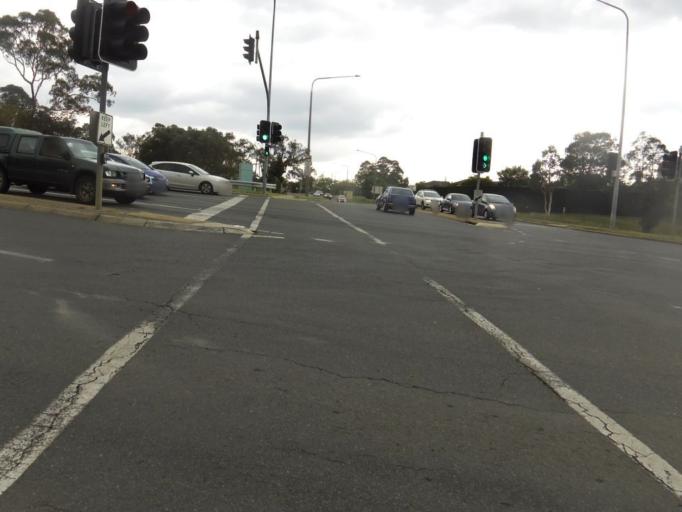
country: AU
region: Australian Capital Territory
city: Forrest
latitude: -35.3445
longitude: 149.1387
